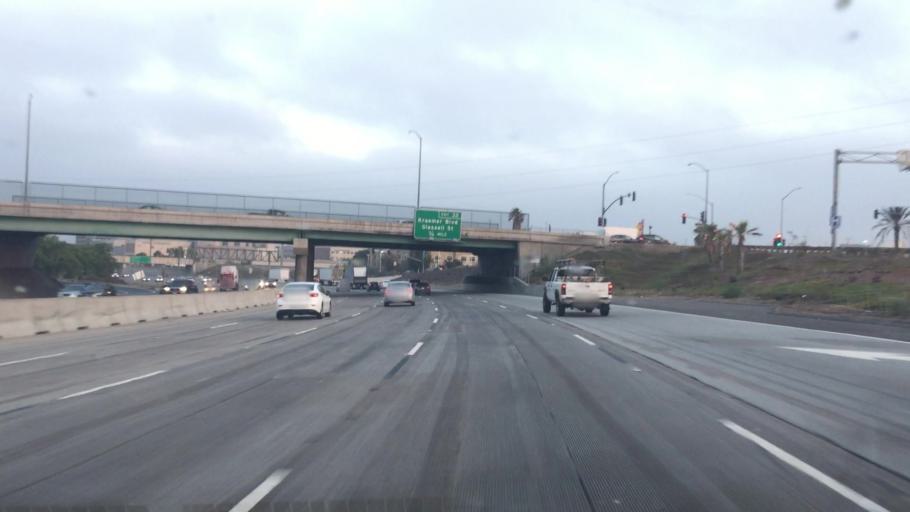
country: US
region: California
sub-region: Orange County
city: Placentia
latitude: 33.8508
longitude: -117.8369
